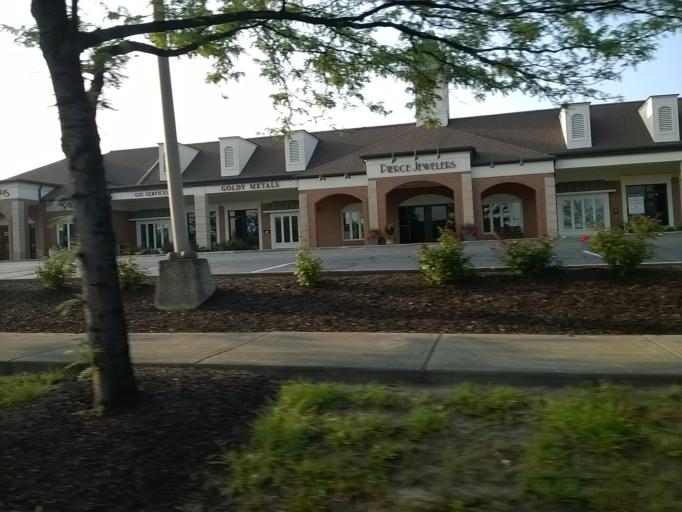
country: US
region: Indiana
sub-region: Hamilton County
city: Carmel
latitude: 39.9615
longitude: -86.1252
